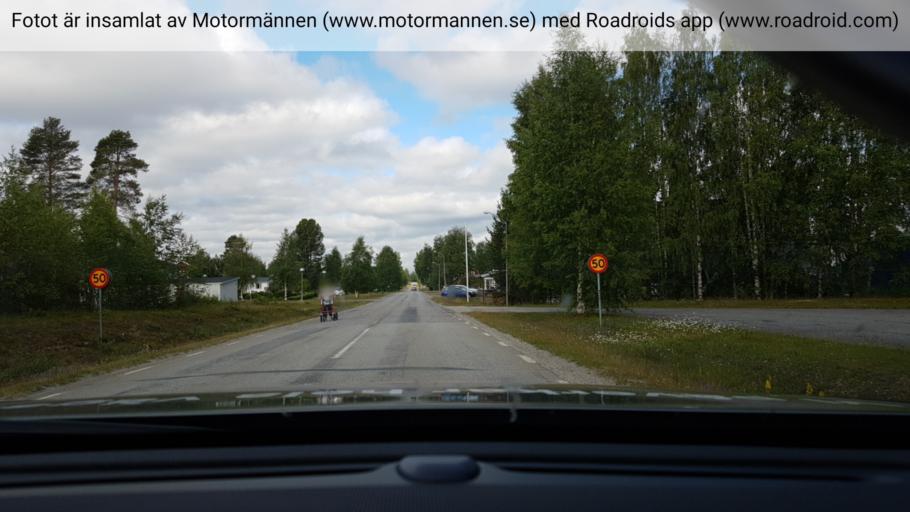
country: SE
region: Vaesterbotten
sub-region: Lycksele Kommun
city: Lycksele
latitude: 64.8133
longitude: 18.9090
